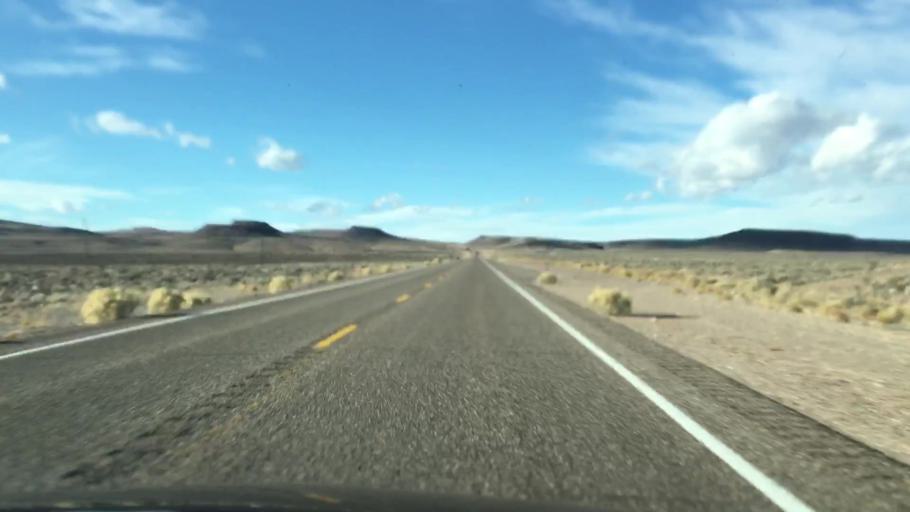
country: US
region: Nevada
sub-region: Esmeralda County
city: Goldfield
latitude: 37.3665
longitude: -117.1221
